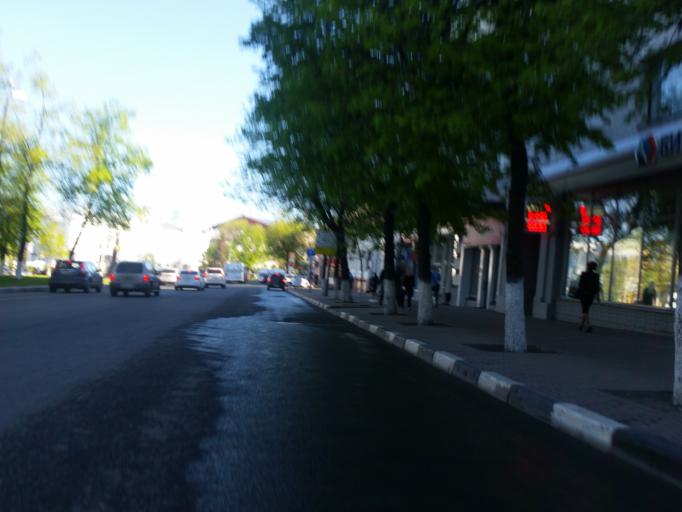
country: RU
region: Ulyanovsk
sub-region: Ulyanovskiy Rayon
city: Ulyanovsk
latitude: 54.3152
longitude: 48.3960
